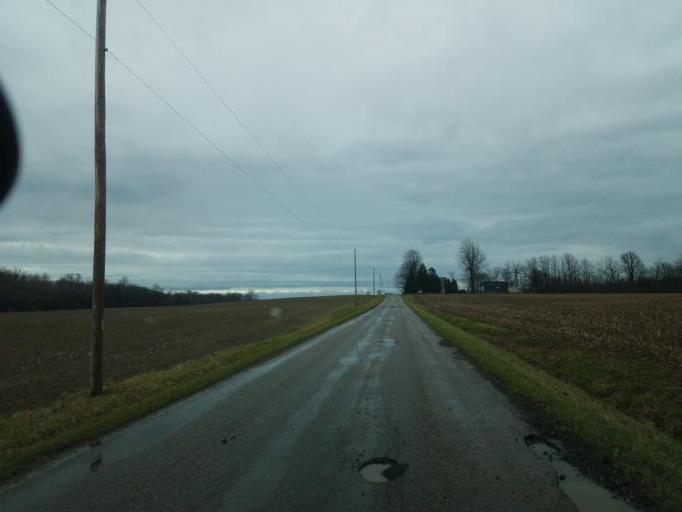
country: US
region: Ohio
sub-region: Richland County
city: Lexington
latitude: 40.6629
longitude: -82.6717
